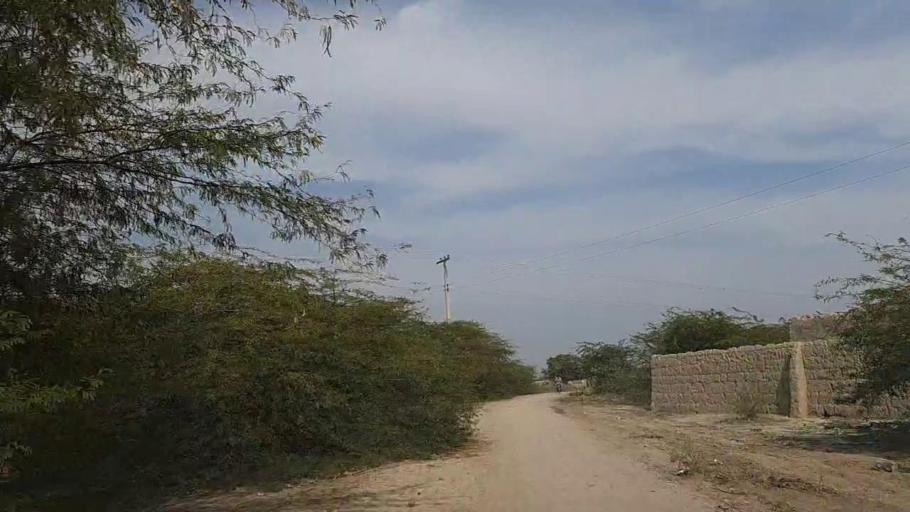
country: PK
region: Sindh
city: Daur
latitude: 26.4277
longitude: 68.4537
